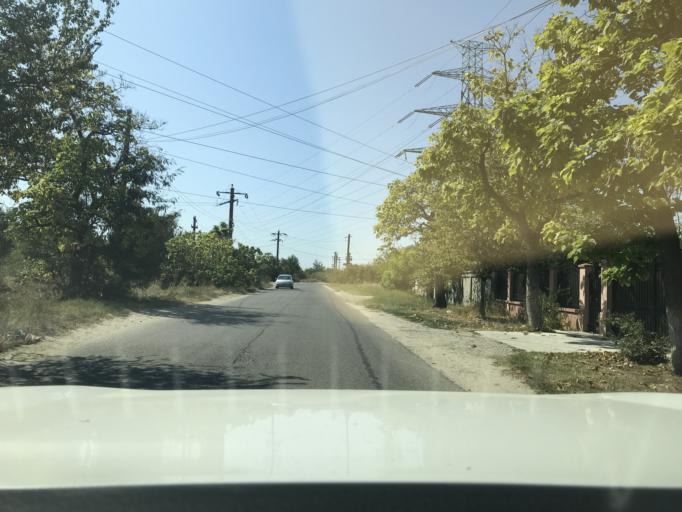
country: RO
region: Olt
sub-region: Municipiul Slatina
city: Slatina
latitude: 44.4164
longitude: 24.3629
